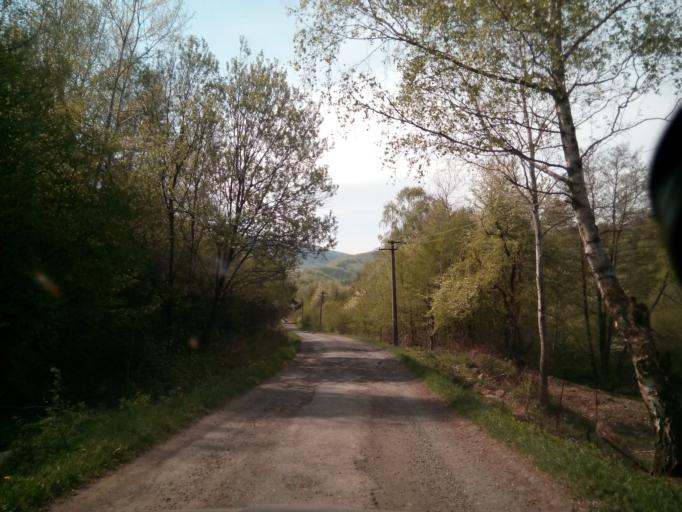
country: SK
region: Presovsky
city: Giraltovce
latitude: 48.9722
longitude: 21.5047
